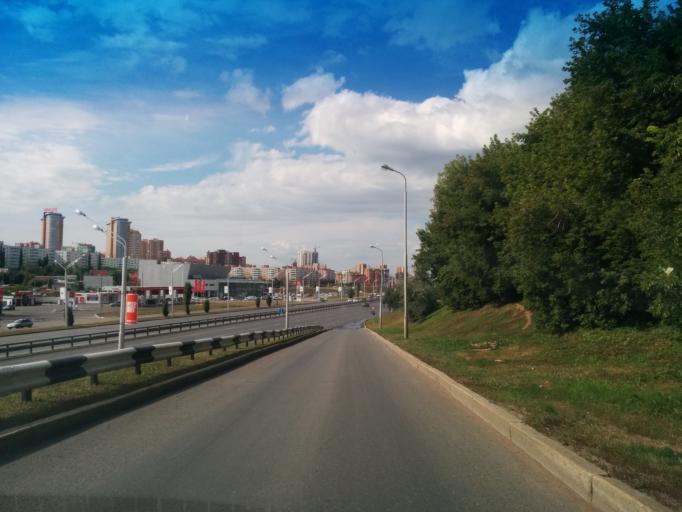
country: RU
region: Bashkortostan
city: Ufa
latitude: 54.7282
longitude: 55.9927
